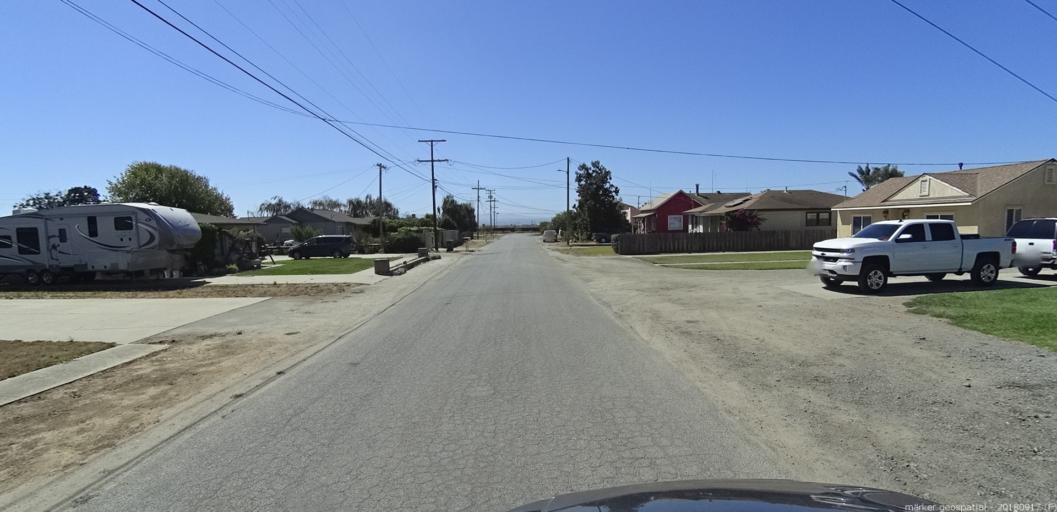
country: US
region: California
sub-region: Monterey County
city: Prunedale
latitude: 36.7506
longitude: -121.6203
